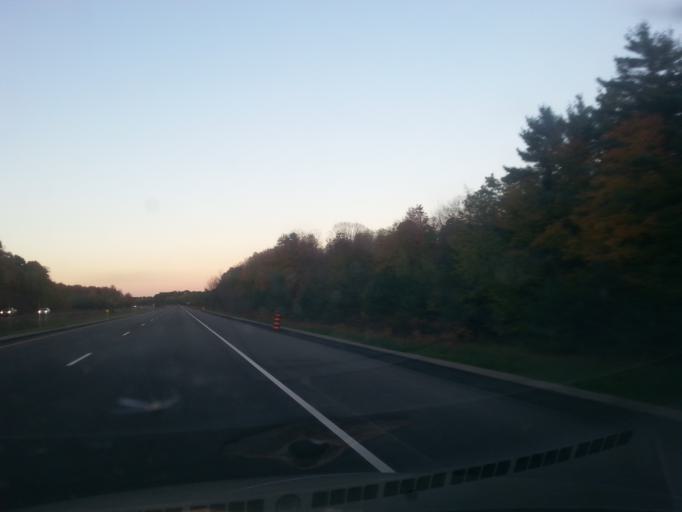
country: CA
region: Ontario
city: Barrie
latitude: 44.5918
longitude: -79.6832
